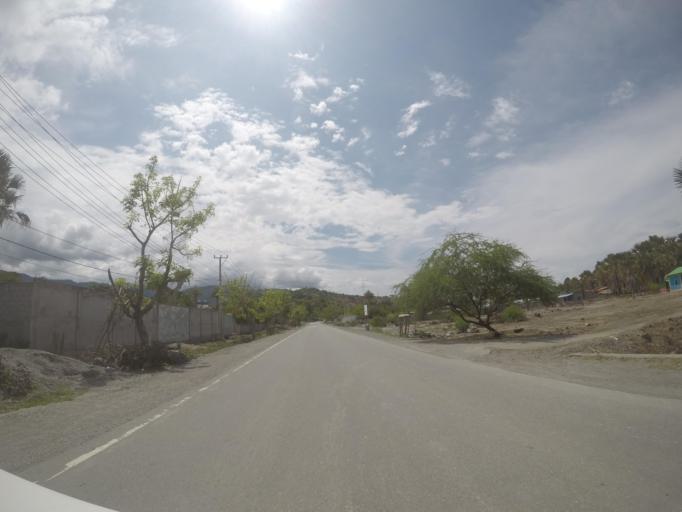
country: TL
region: Dili
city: Dili
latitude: -8.5726
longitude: 125.4608
